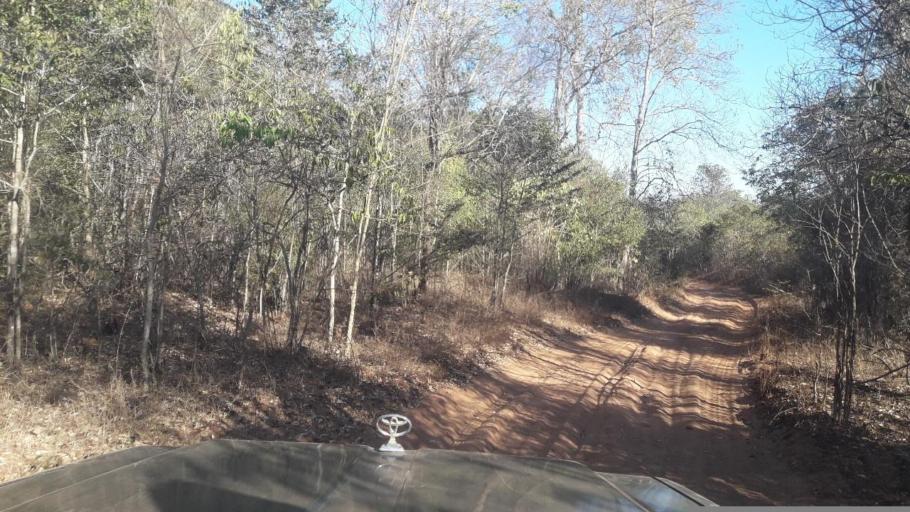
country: MG
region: Boeny
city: Sitampiky
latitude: -16.4216
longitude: 45.6188
